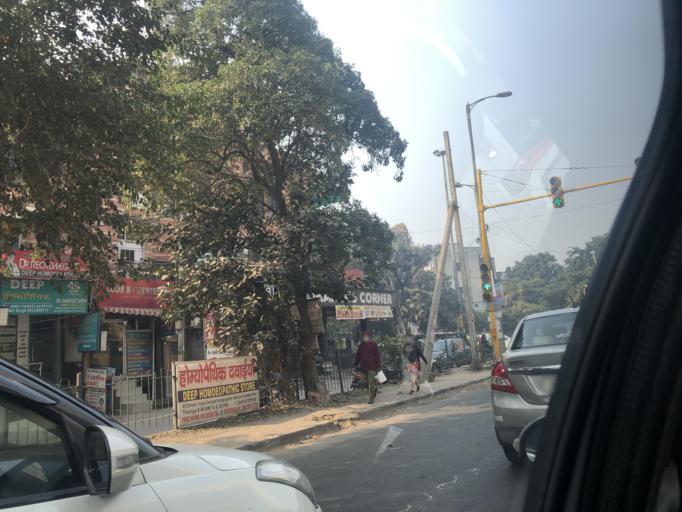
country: IN
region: NCT
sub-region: North West Delhi
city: Pitampura
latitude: 28.6781
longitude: 77.1053
